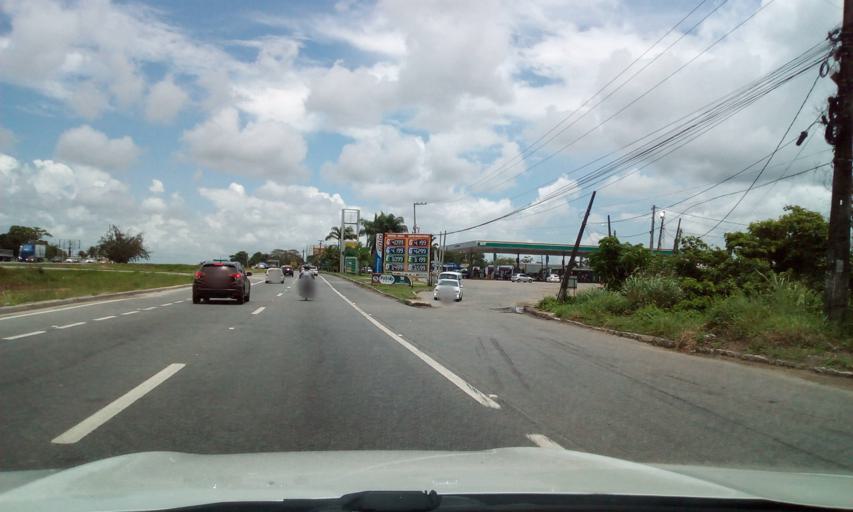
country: BR
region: Pernambuco
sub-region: Paulista
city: Paulista
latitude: -7.9623
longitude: -34.9145
